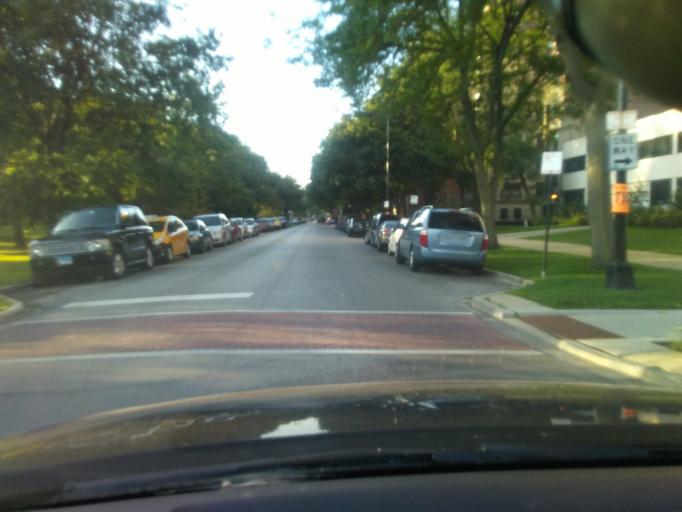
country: US
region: Illinois
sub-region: Cook County
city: Evanston
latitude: 41.9743
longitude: -87.6514
